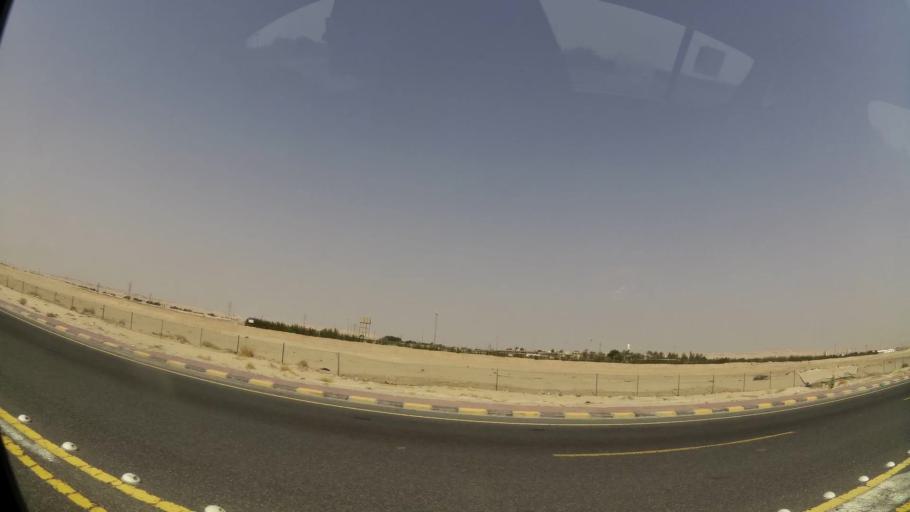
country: KW
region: Muhafazat al Jahra'
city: Al Jahra'
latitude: 29.3699
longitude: 47.6548
